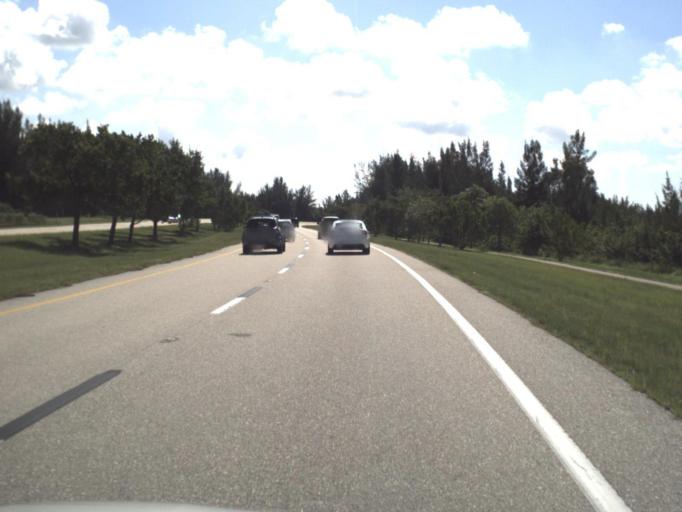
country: US
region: Florida
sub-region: Lee County
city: Pine Island Center
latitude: 26.6156
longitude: -82.0396
